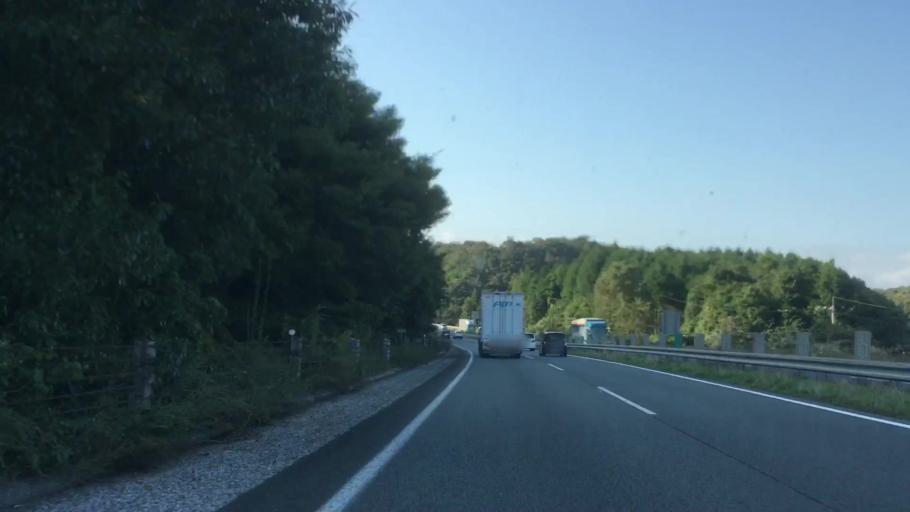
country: JP
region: Yamaguchi
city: Ogori-shimogo
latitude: 34.1586
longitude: 131.3316
